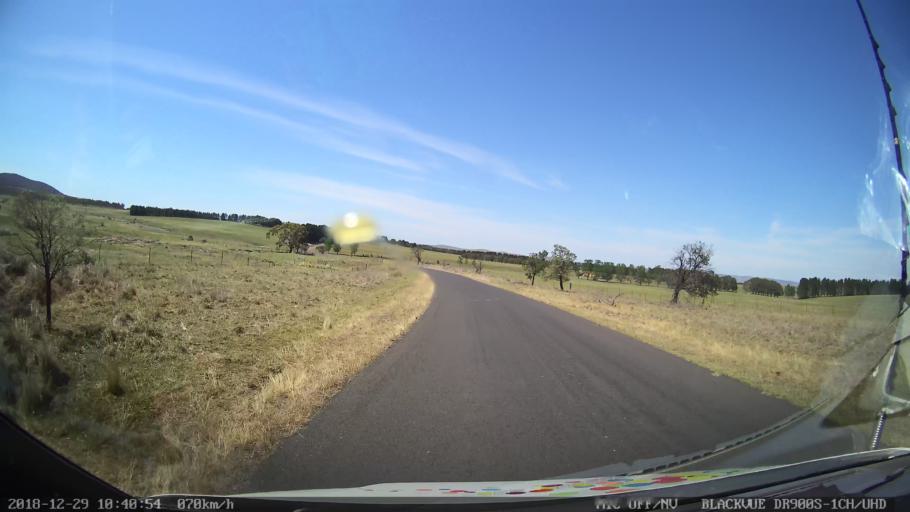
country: AU
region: New South Wales
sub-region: Palerang
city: Bungendore
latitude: -35.0196
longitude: 149.5194
